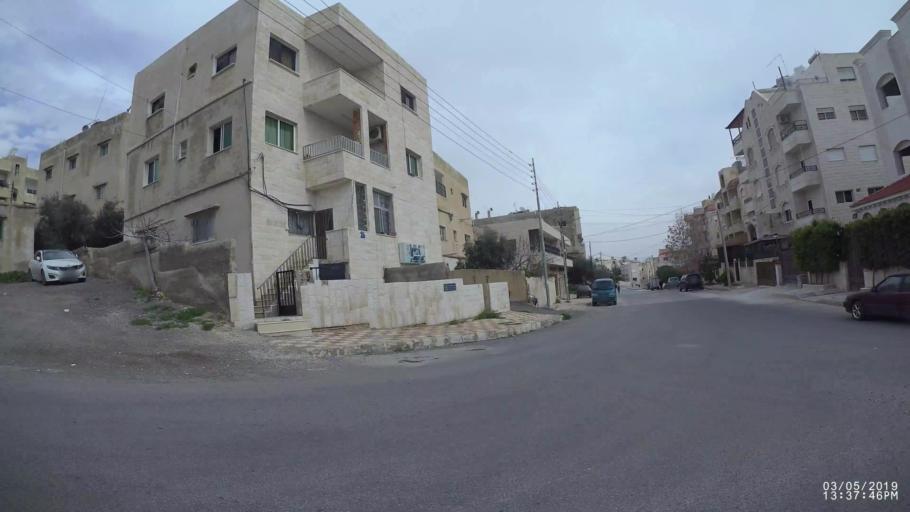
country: JO
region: Amman
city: Amman
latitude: 31.9981
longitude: 35.9420
